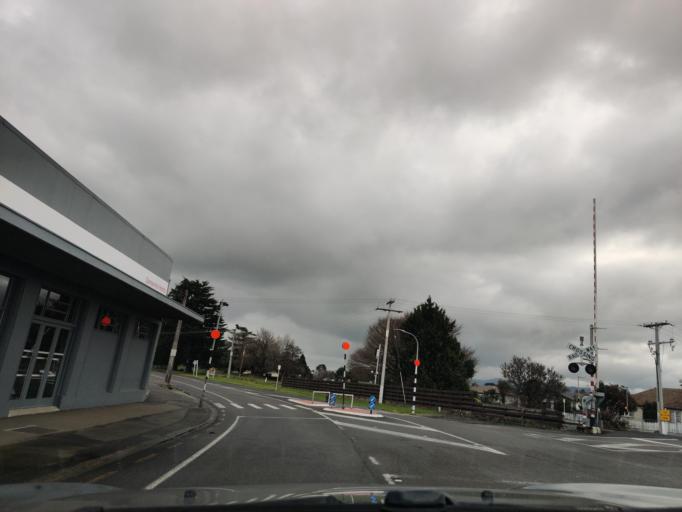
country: NZ
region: Manawatu-Wanganui
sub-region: Palmerston North City
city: Palmerston North
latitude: -40.2103
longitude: 176.0944
